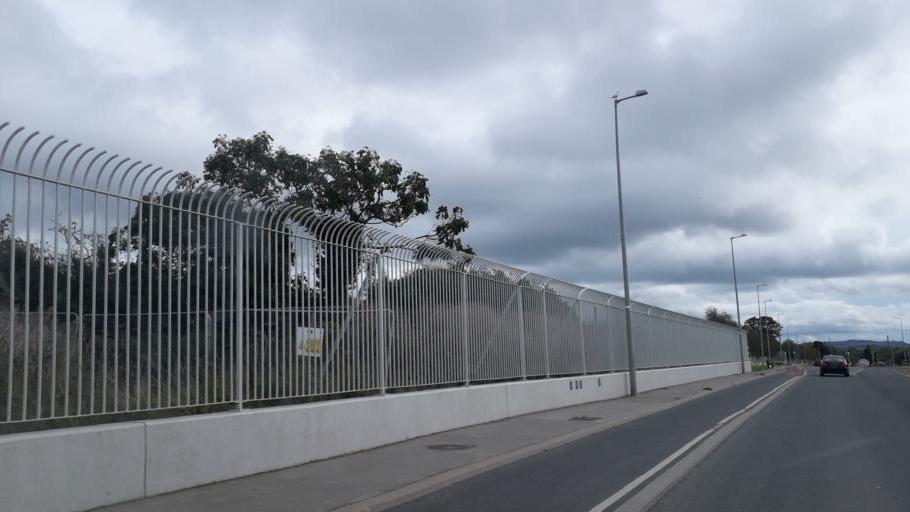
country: IE
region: Leinster
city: Cabinteely
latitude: 53.2738
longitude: -6.1536
